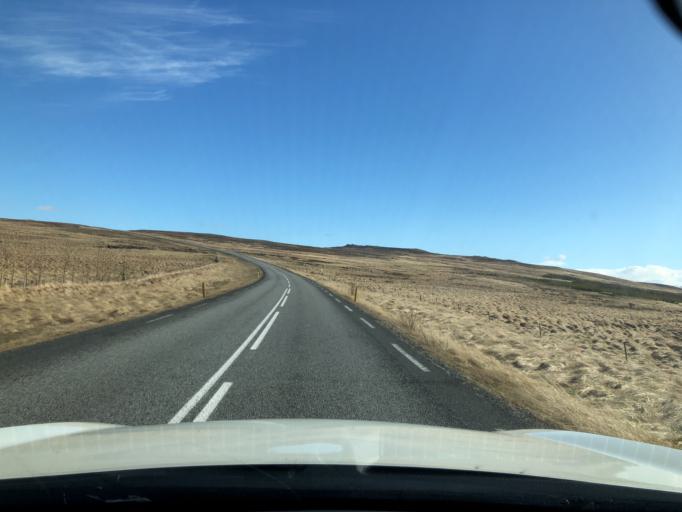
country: IS
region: Capital Region
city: Mosfellsbaer
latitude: 64.6648
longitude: -21.2690
